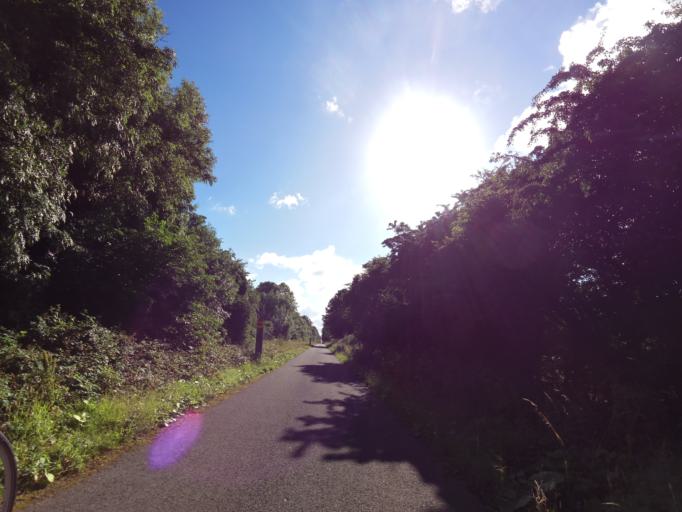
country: IE
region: Leinster
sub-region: Uibh Fhaili
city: Clara
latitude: 53.4175
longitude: -7.6354
